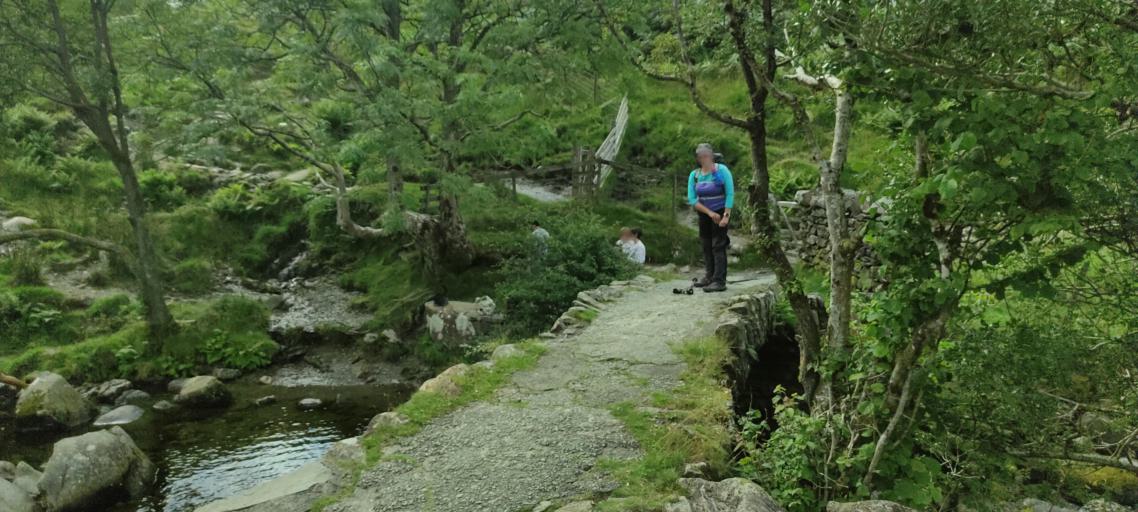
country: GB
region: England
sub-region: Cumbria
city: Ambleside
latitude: 54.4524
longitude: -2.9590
